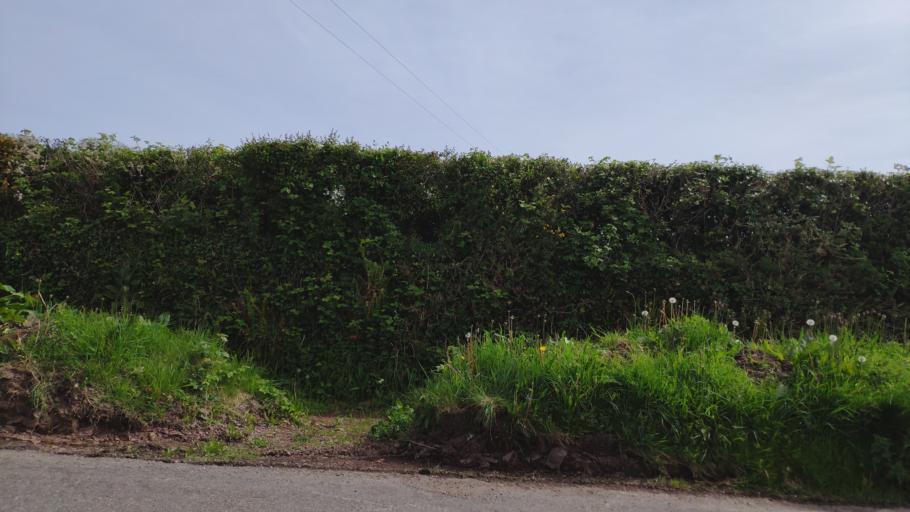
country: IE
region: Munster
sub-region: County Cork
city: Blarney
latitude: 51.9573
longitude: -8.5094
